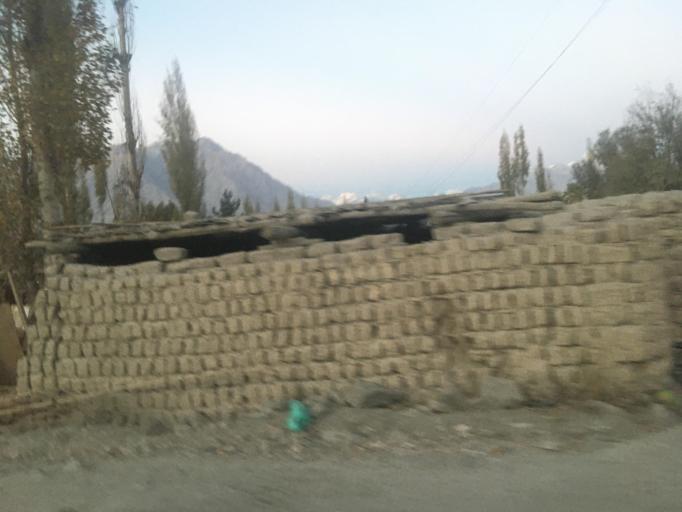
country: PK
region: Gilgit-Baltistan
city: Skardu
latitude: 35.2943
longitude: 75.5703
